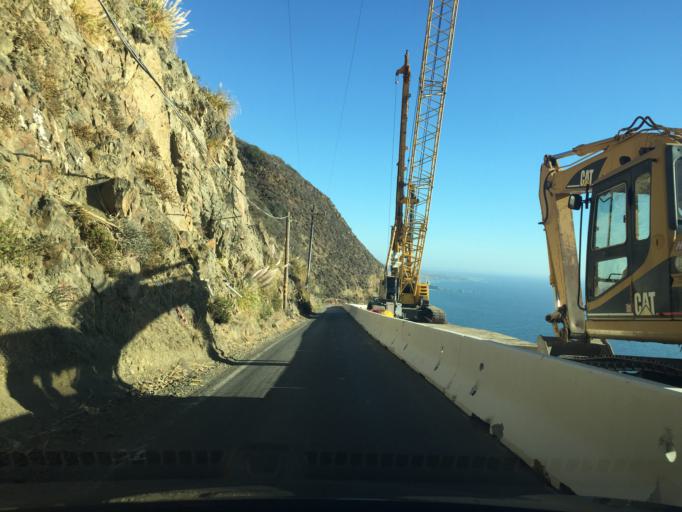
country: US
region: California
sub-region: San Luis Obispo County
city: Cambria
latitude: 35.7921
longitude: -121.3403
